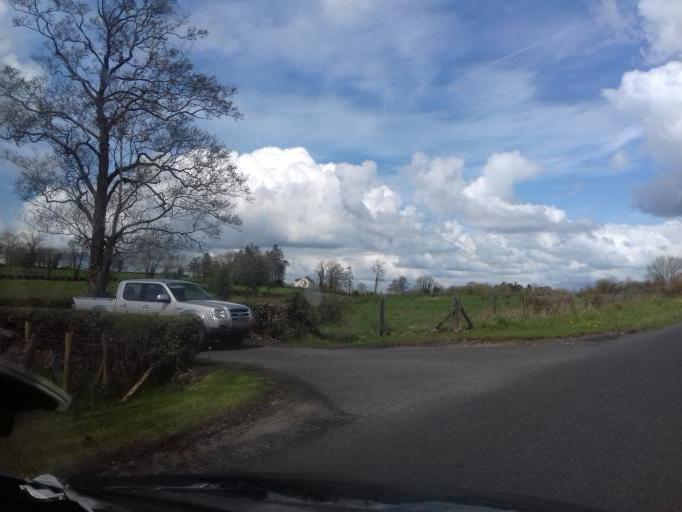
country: GB
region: Northern Ireland
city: Lisnaskea
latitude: 54.1809
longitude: -7.5010
